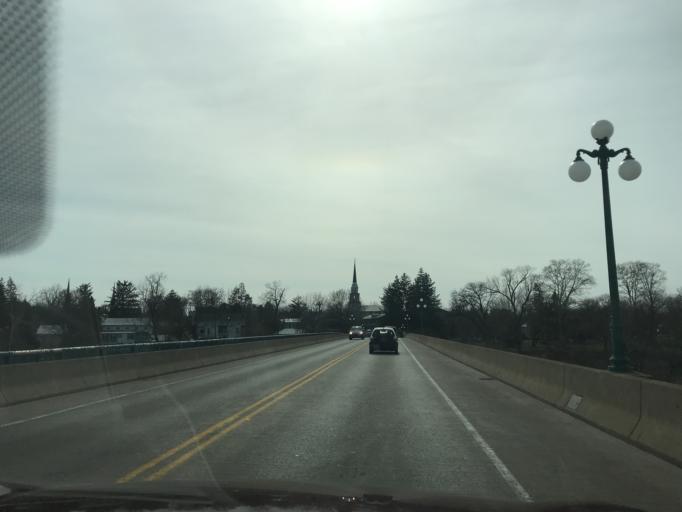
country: US
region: Pennsylvania
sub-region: Union County
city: Lewisburg
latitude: 40.9670
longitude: -76.8789
